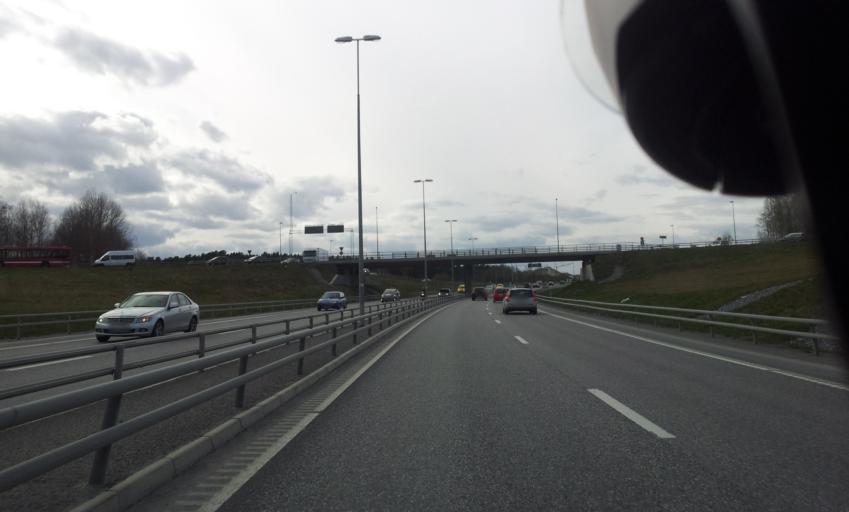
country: SE
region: Stockholm
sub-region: Jarfalla Kommun
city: Jakobsberg
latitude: 59.4002
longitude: 17.8849
